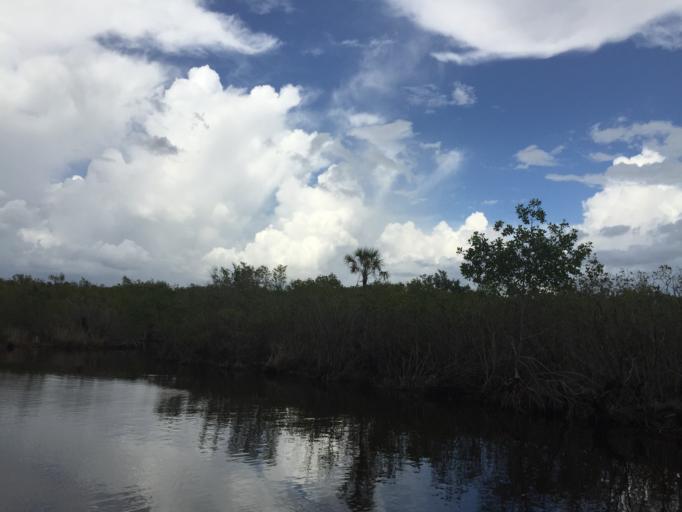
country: US
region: Florida
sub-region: Collier County
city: Marco
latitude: 25.8981
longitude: -81.3731
